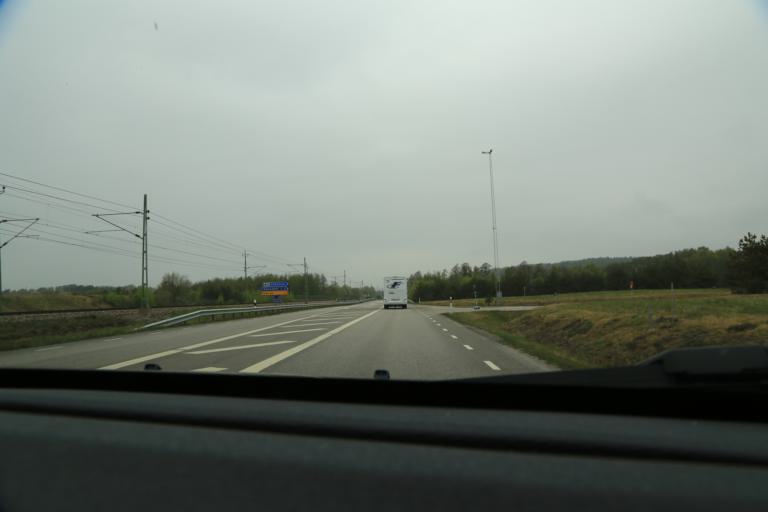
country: SE
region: Halland
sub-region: Varbergs Kommun
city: Varberg
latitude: 57.1810
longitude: 12.2266
